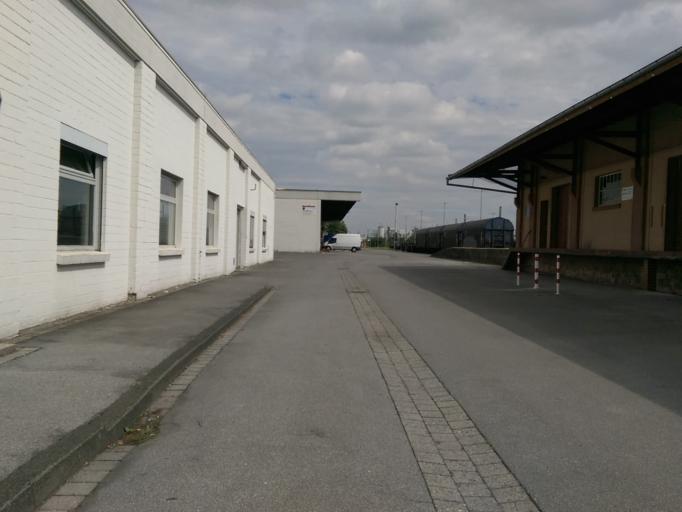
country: DE
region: North Rhine-Westphalia
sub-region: Regierungsbezirk Detmold
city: Guetersloh
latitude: 51.9091
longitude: 8.3866
